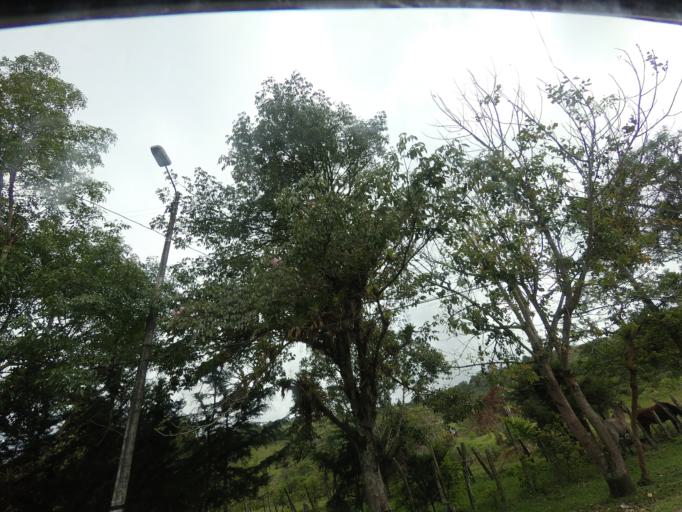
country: CO
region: Huila
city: San Agustin
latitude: 1.8870
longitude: -76.2782
